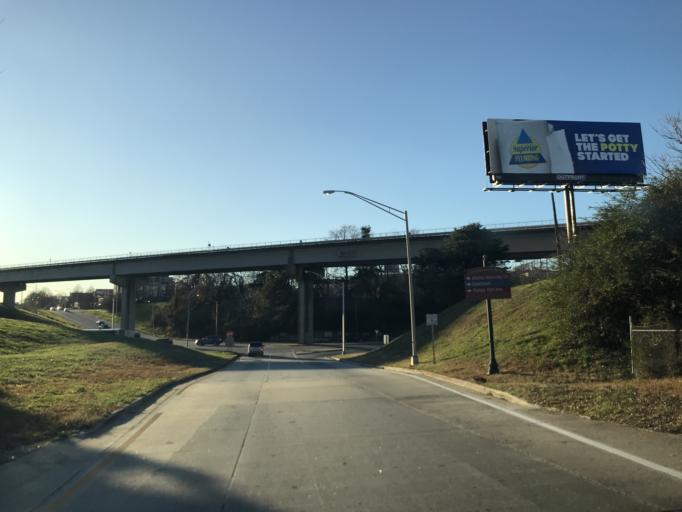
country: US
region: Georgia
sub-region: Fulton County
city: Atlanta
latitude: 33.7460
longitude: -84.3968
